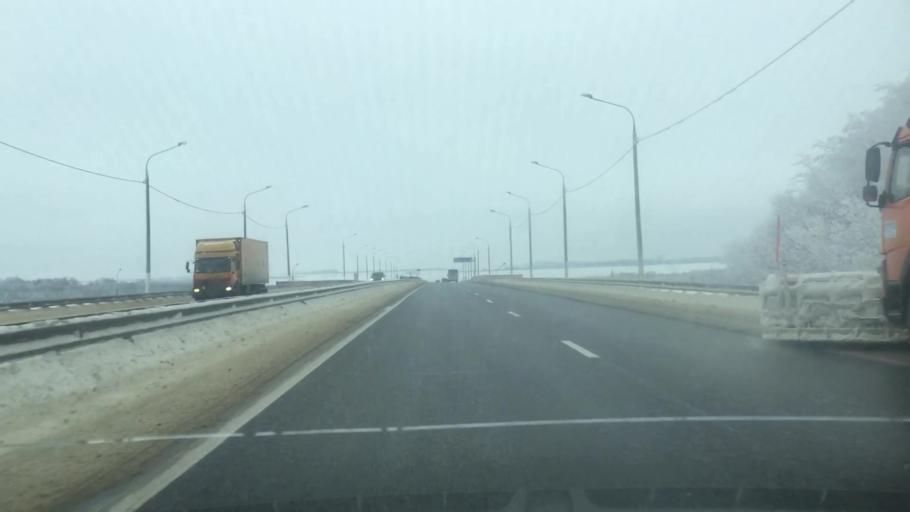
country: RU
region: Tula
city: Kazachka
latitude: 53.2898
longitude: 38.1786
